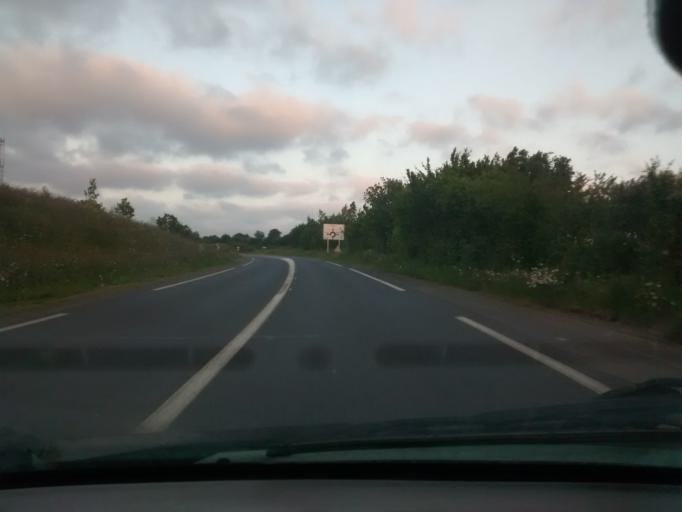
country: FR
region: Lower Normandy
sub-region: Departement de la Manche
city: Agneaux
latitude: 49.0998
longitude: -1.1136
